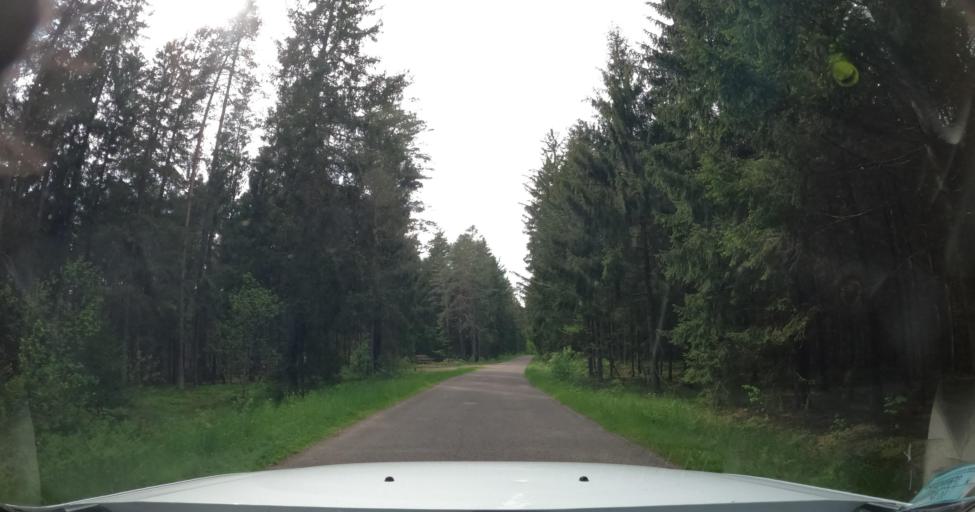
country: PL
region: Warmian-Masurian Voivodeship
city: Dobre Miasto
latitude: 54.0962
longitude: 20.3902
